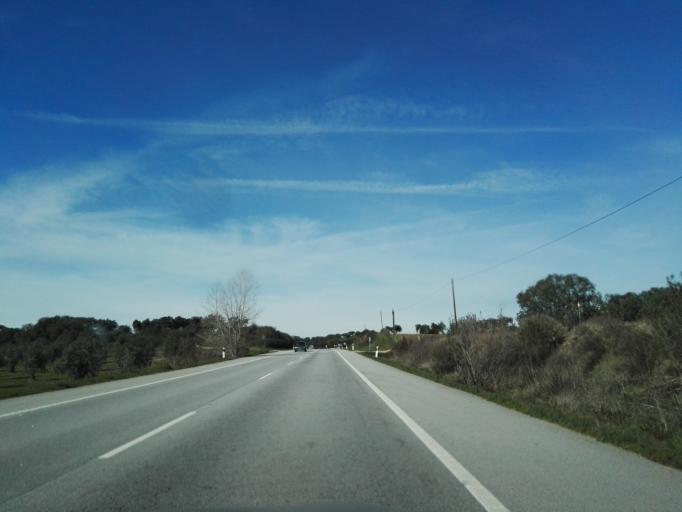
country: PT
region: Portalegre
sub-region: Portalegre
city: Urra
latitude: 39.1938
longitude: -7.3609
